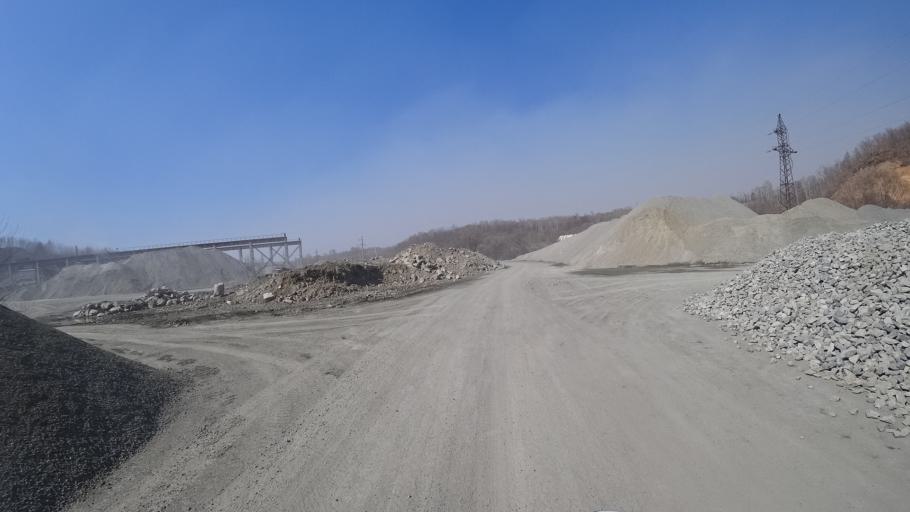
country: RU
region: Amur
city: Novobureyskiy
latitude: 49.7916
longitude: 129.9620
